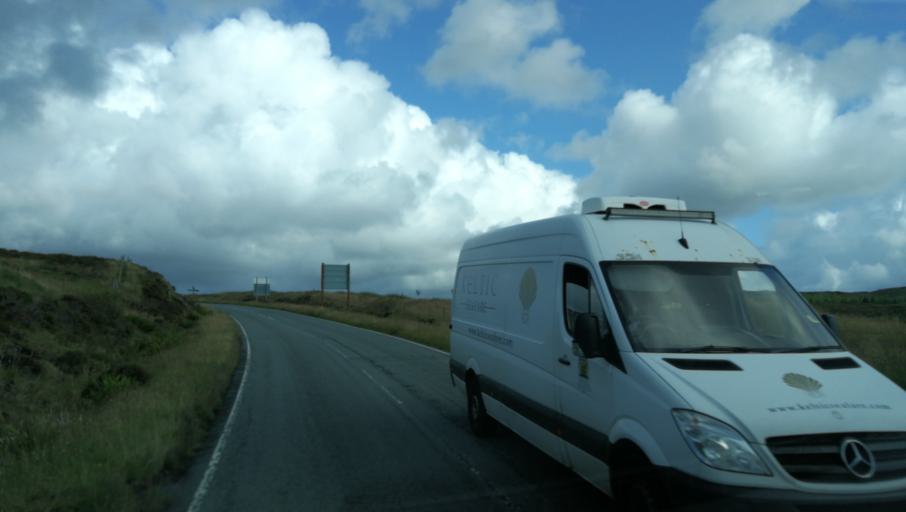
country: GB
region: Scotland
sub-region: Highland
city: Isle of Skye
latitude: 57.4692
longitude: -6.5355
